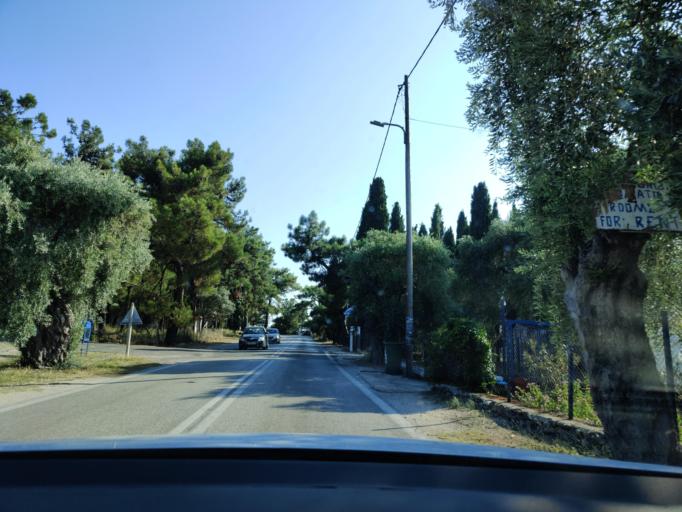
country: GR
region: East Macedonia and Thrace
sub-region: Nomos Kavalas
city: Prinos
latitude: 40.6972
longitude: 24.5260
